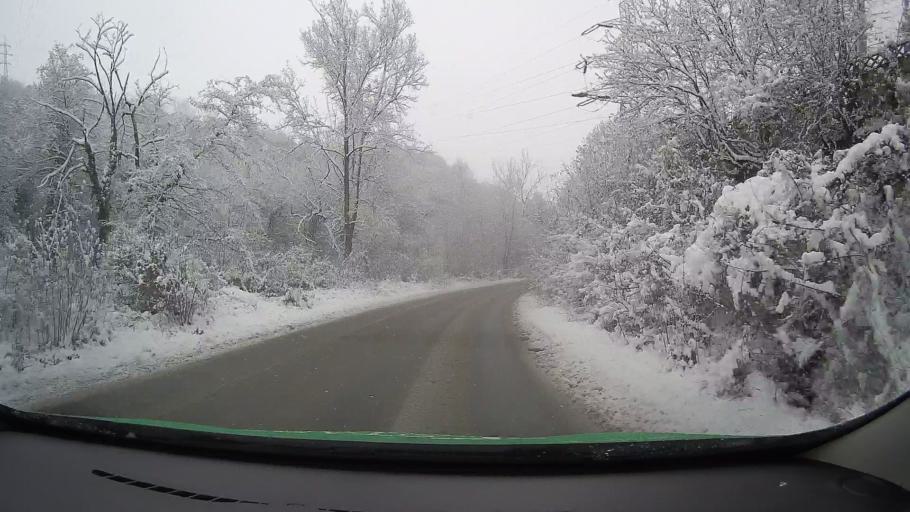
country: RO
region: Hunedoara
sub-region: Comuna Teliucu Inferior
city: Teliucu Inferior
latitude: 45.7299
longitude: 22.8820
